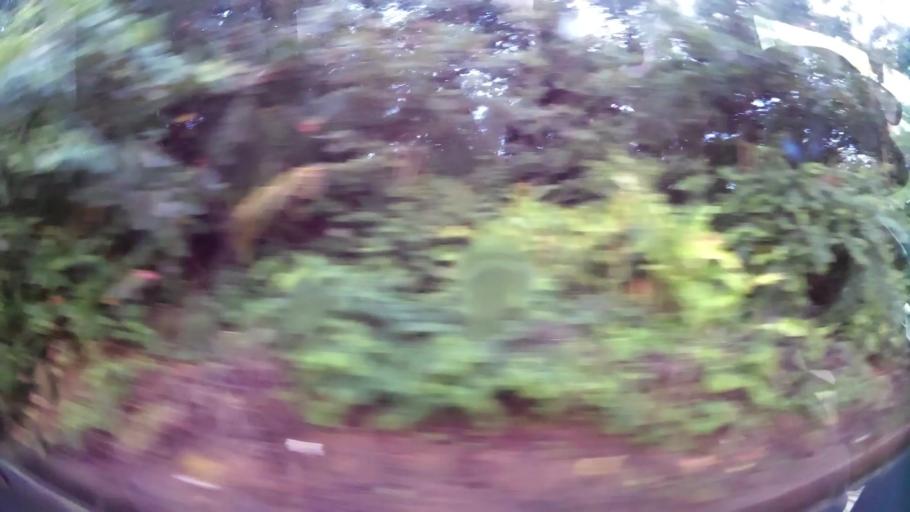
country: DM
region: Saint Andrew
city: Marigot
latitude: 15.5419
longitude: -61.2880
